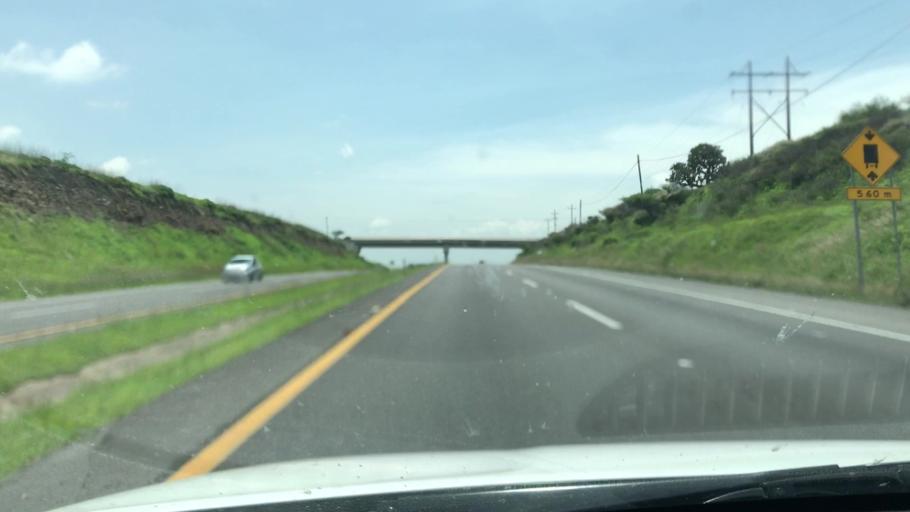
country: MX
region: Guanajuato
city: Penjamo
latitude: 20.3840
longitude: -101.7943
